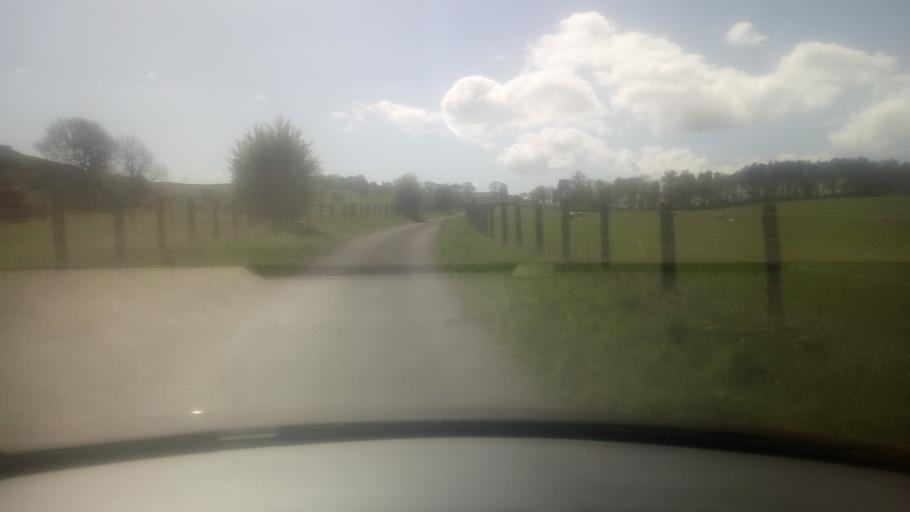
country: GB
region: Scotland
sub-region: The Scottish Borders
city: Hawick
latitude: 55.4239
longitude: -2.7100
